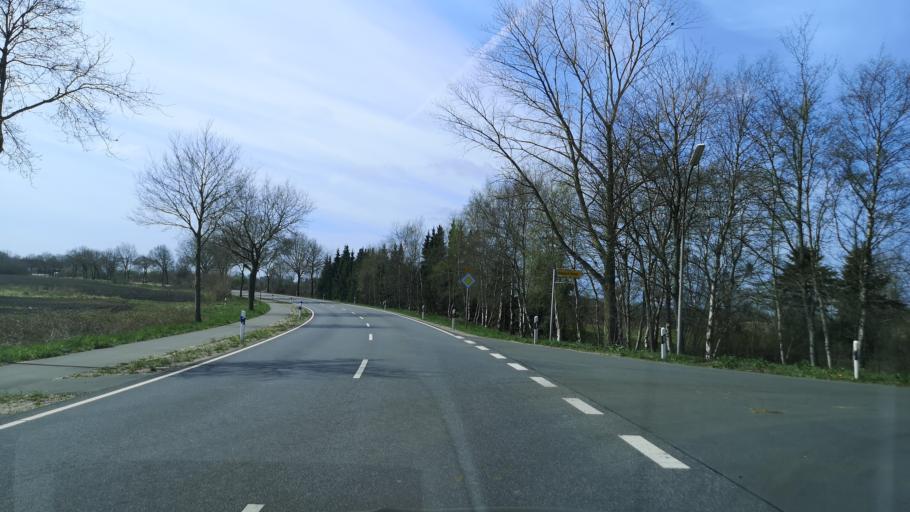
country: DE
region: Schleswig-Holstein
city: Hamdorf
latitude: 54.2283
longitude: 9.5021
